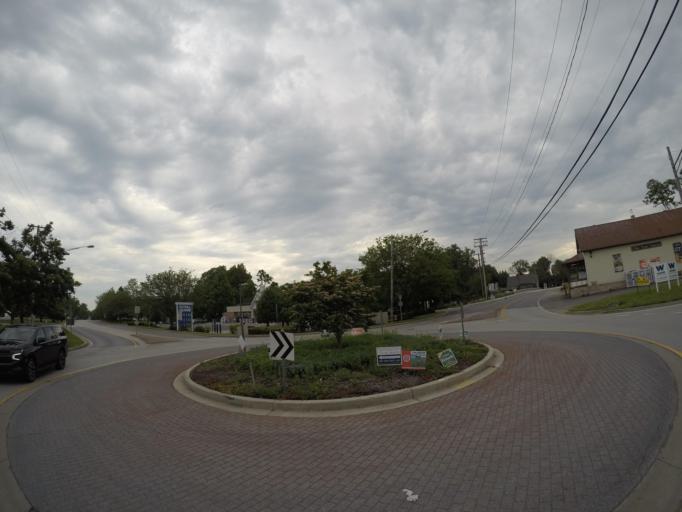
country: US
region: Maryland
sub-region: Howard County
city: Highland
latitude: 39.2633
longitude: -76.9864
